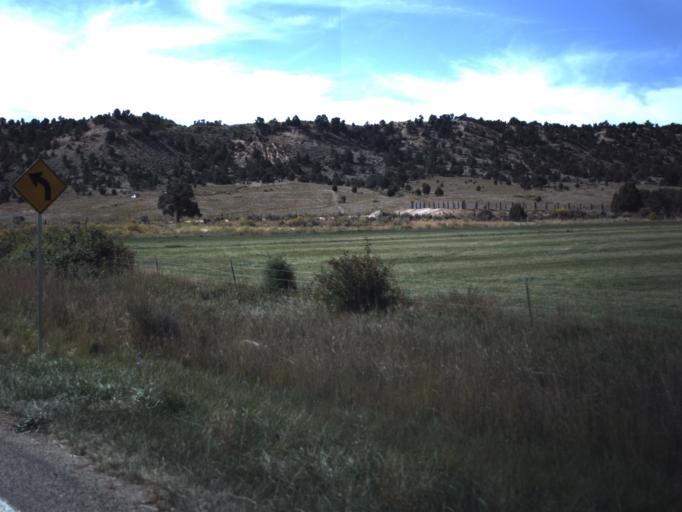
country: US
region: Utah
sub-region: Garfield County
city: Panguitch
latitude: 37.6186
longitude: -112.0772
